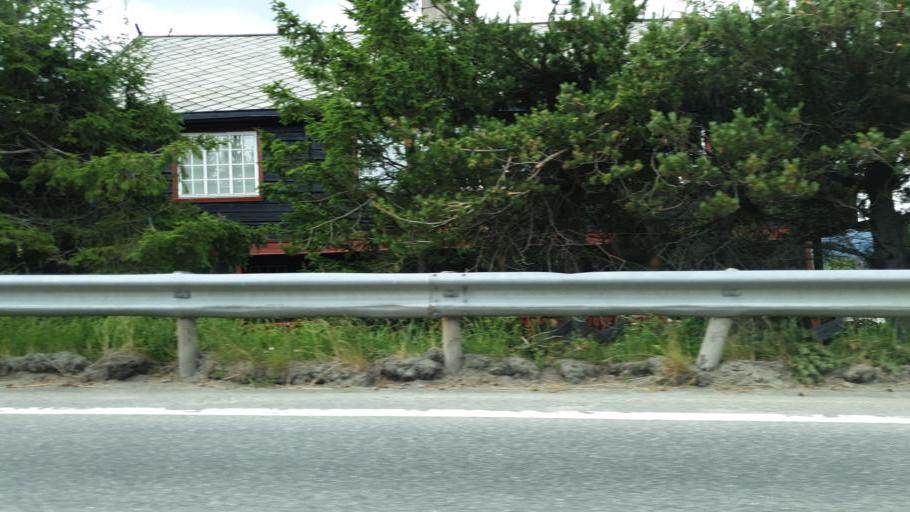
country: NO
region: Sor-Trondelag
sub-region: Oppdal
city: Oppdal
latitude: 62.5337
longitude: 9.6176
